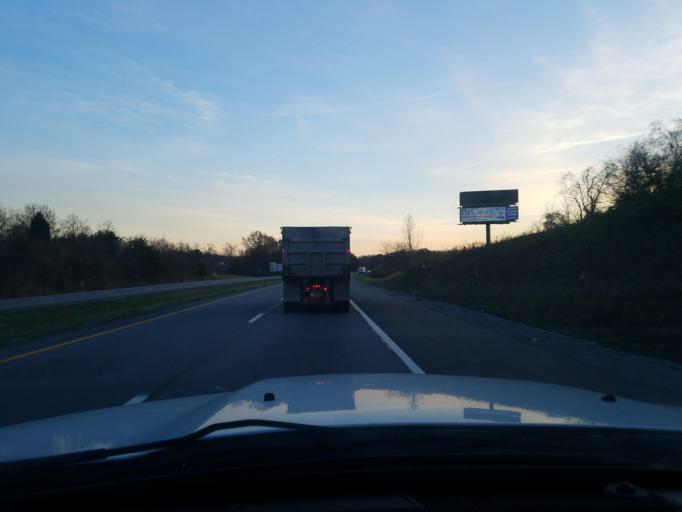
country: US
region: West Virginia
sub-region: Wood County
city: Williamstown
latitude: 39.3731
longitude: -81.4396
